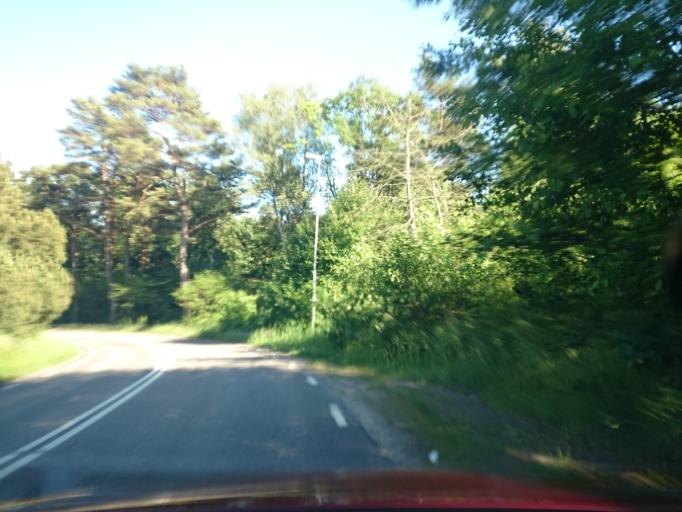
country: SE
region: Vaestra Goetaland
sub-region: Lerums Kommun
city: Lerum
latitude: 57.7758
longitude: 12.2576
